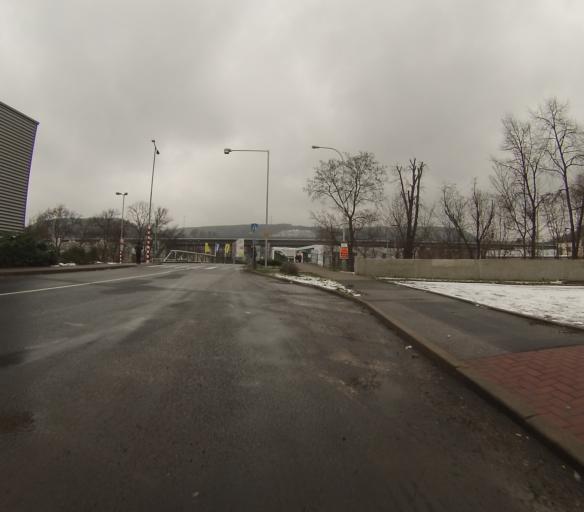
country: CZ
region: Ustecky
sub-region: Okres Decin
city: Decin
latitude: 50.7753
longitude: 14.2181
